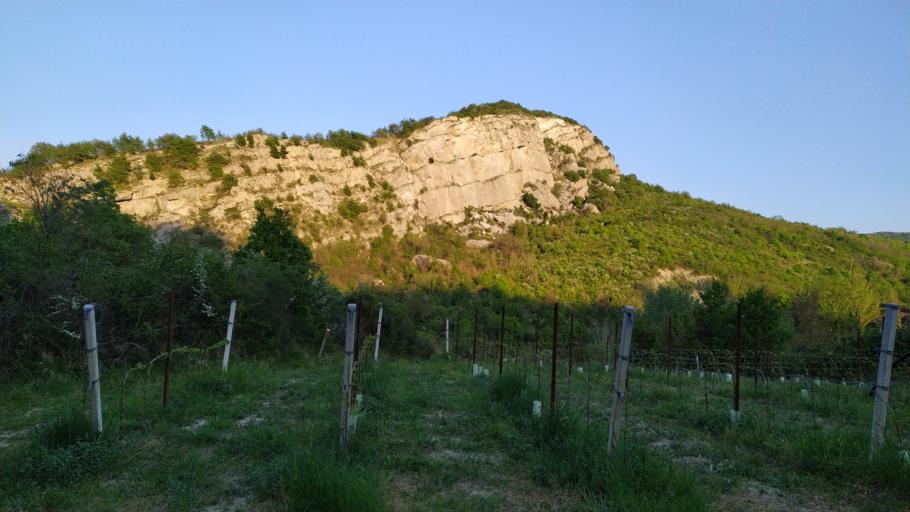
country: IT
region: Emilia-Romagna
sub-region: Provincia di Bologna
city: Borgo Tossignano
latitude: 44.2704
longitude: 11.6088
